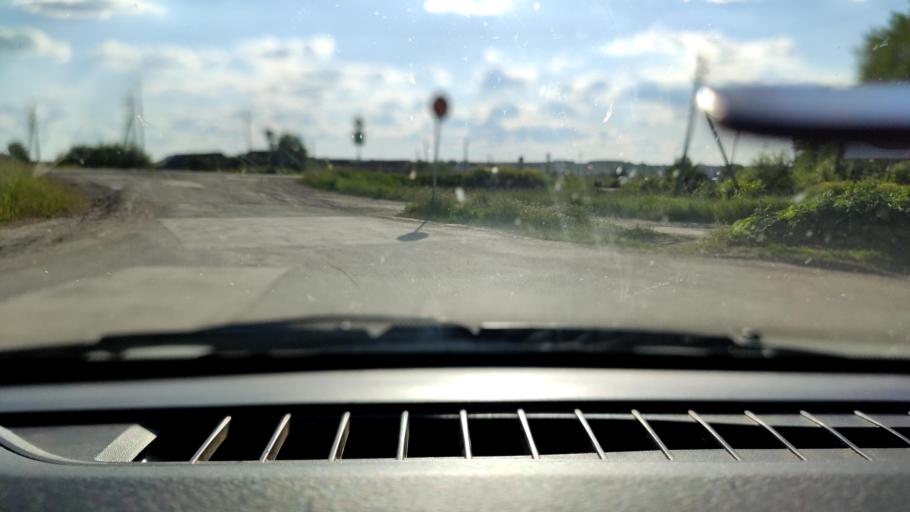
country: RU
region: Perm
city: Orda
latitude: 57.1875
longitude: 56.9167
